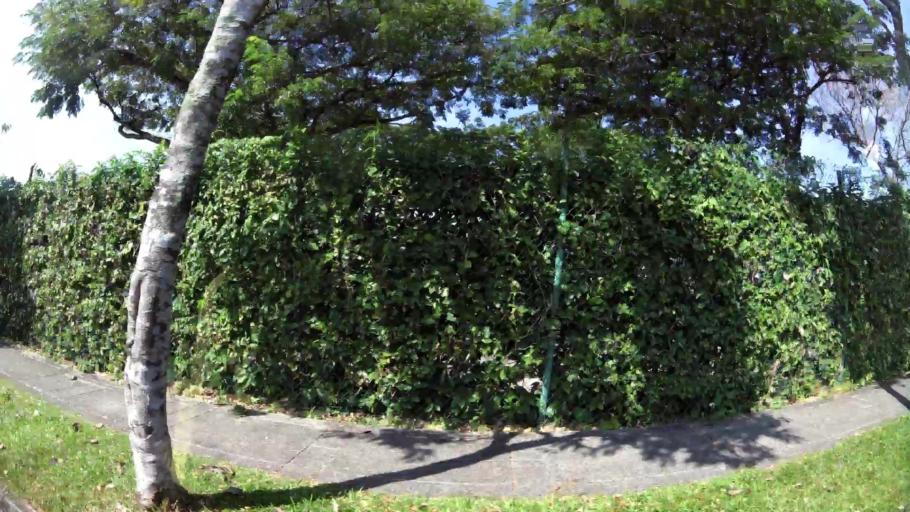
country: SG
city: Singapore
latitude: 1.3743
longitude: 103.8295
